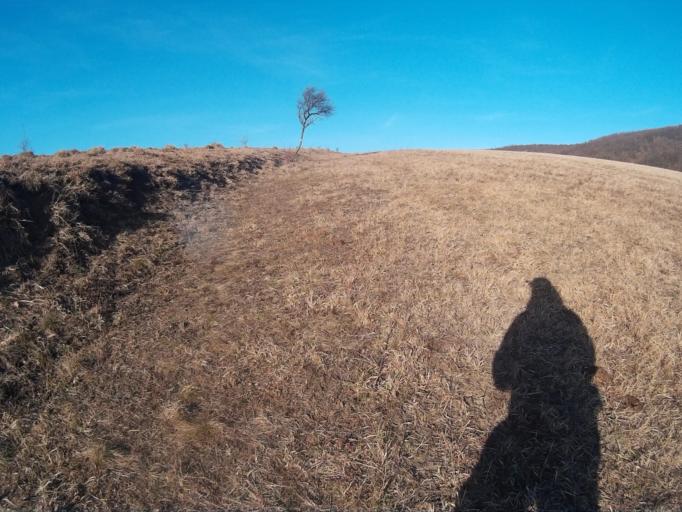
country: HU
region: Borsod-Abauj-Zemplen
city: Putnok
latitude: 48.3992
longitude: 20.4869
